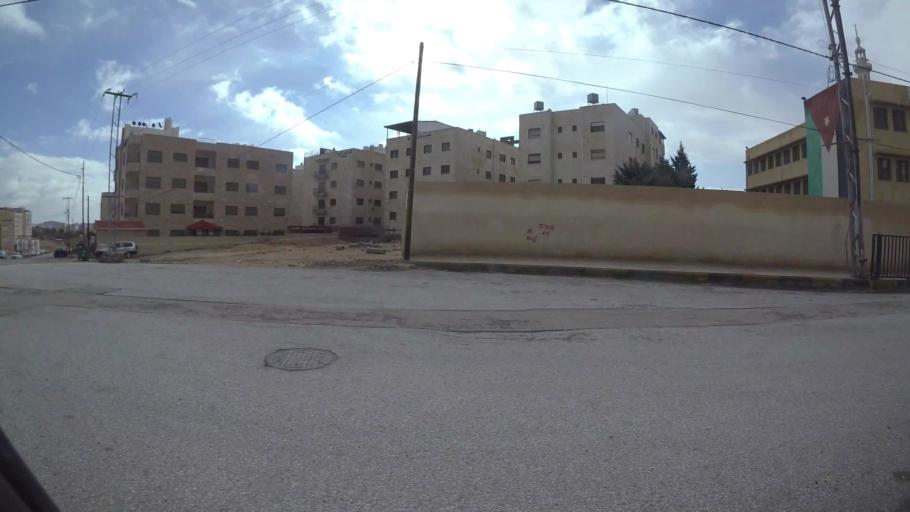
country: JO
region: Amman
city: Al Jubayhah
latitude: 32.0560
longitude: 35.8917
